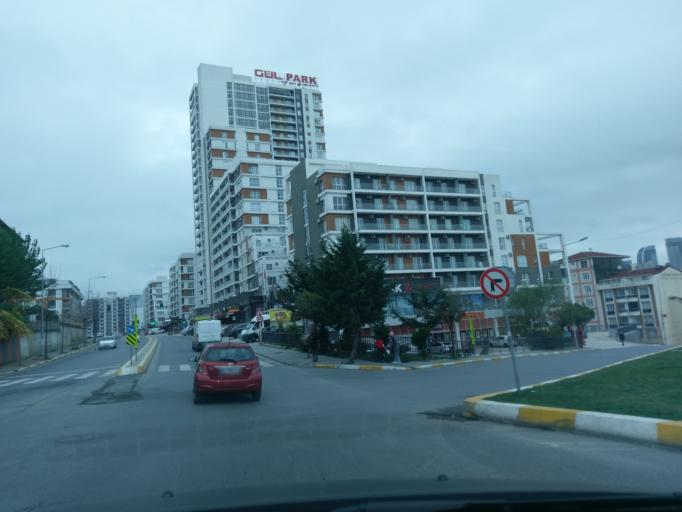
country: TR
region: Istanbul
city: Esenyurt
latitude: 41.0085
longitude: 28.6686
